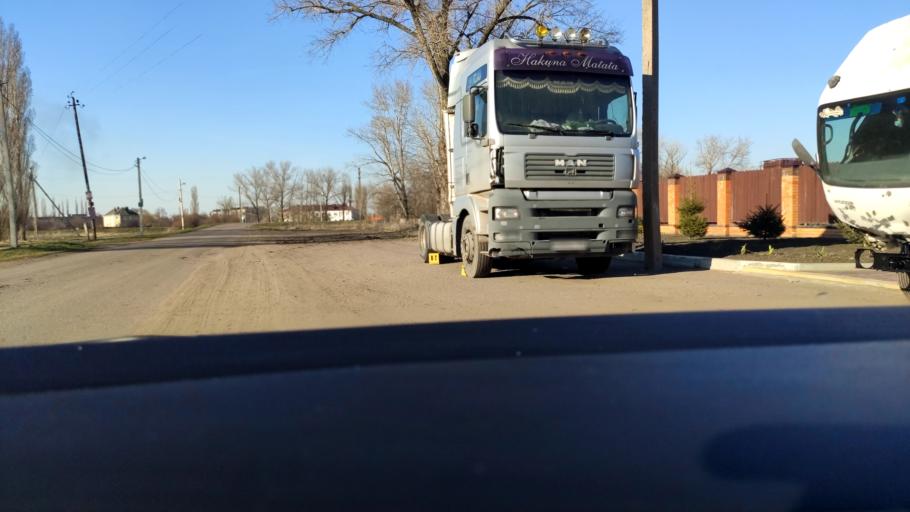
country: RU
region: Voronezj
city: Maslovka
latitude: 51.5081
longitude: 39.2940
